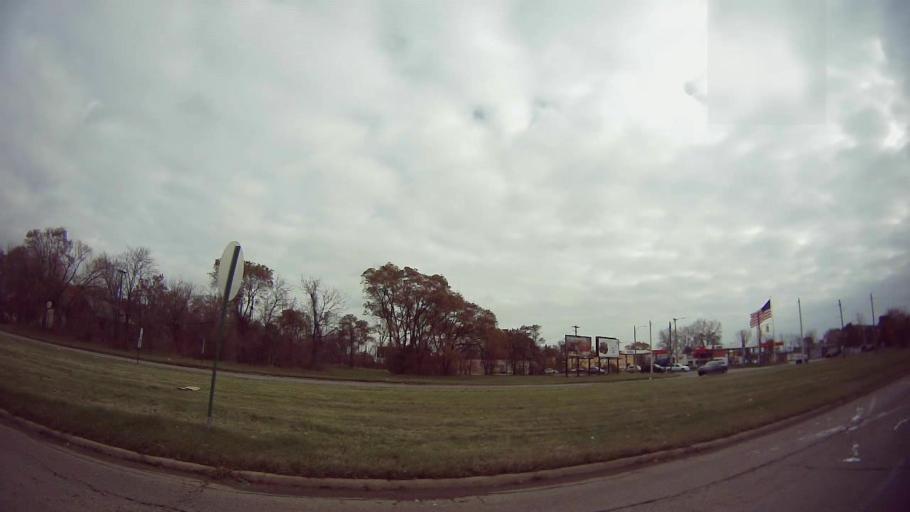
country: US
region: Michigan
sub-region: Wayne County
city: Hamtramck
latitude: 42.4233
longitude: -83.0433
